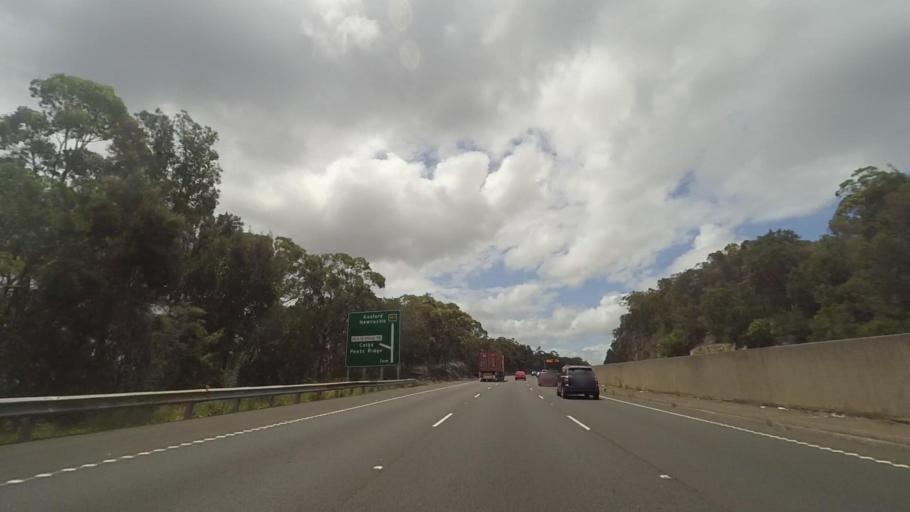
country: AU
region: New South Wales
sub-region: Gosford Shire
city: Point Clare
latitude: -33.4393
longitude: 151.2187
